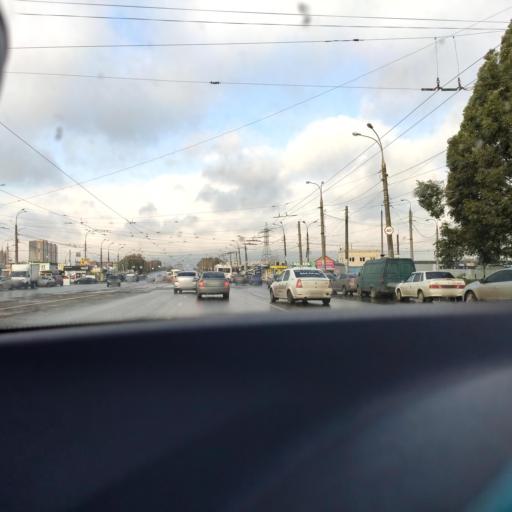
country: RU
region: Samara
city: Smyshlyayevka
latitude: 53.2085
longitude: 50.2760
